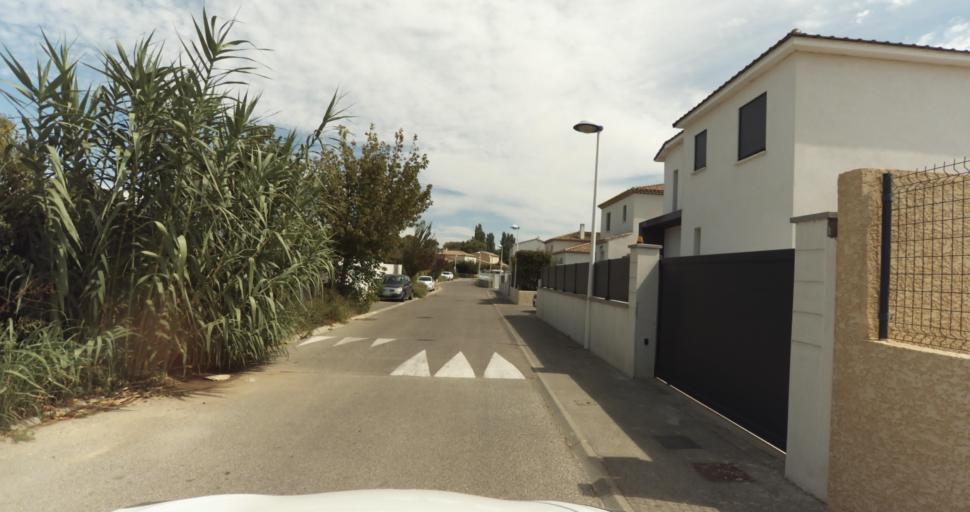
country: FR
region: Provence-Alpes-Cote d'Azur
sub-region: Departement des Bouches-du-Rhone
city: Miramas
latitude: 43.5883
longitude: 5.0153
